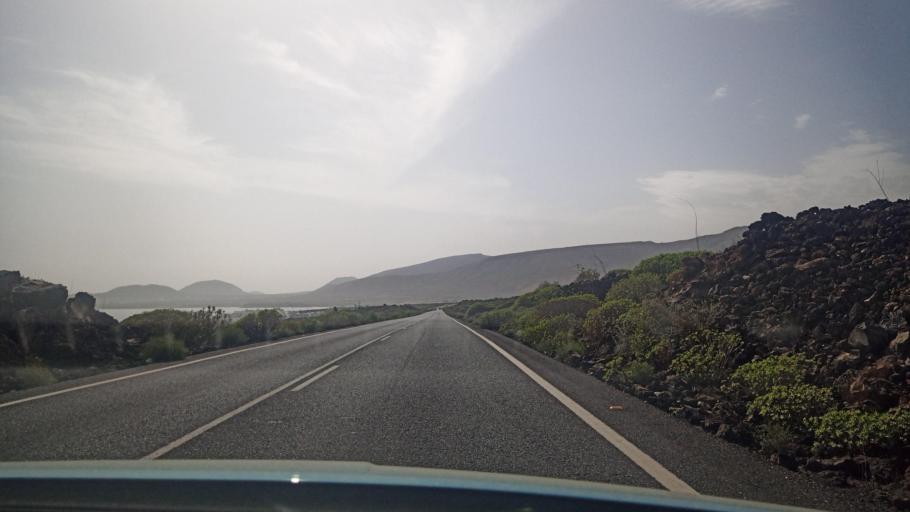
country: ES
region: Canary Islands
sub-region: Provincia de Las Palmas
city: Haria
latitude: 29.1432
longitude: -13.4538
